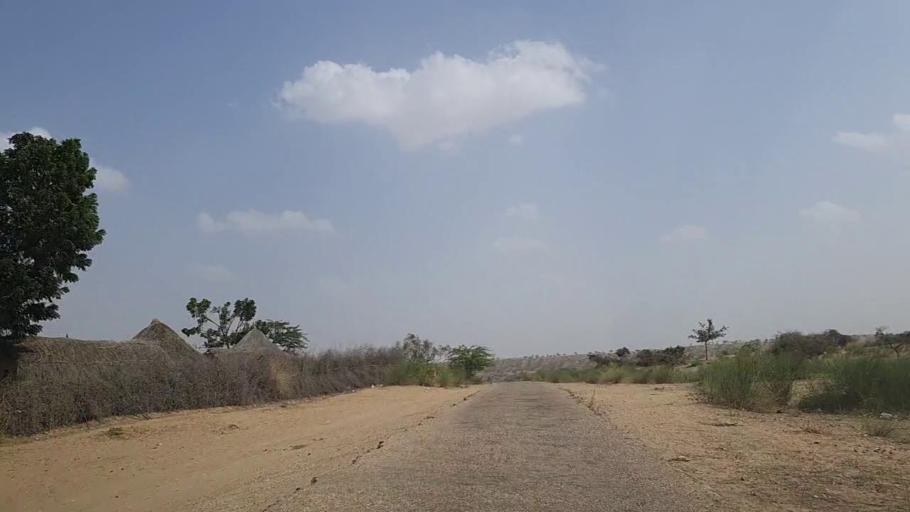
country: PK
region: Sindh
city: Islamkot
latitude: 24.7896
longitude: 70.0856
